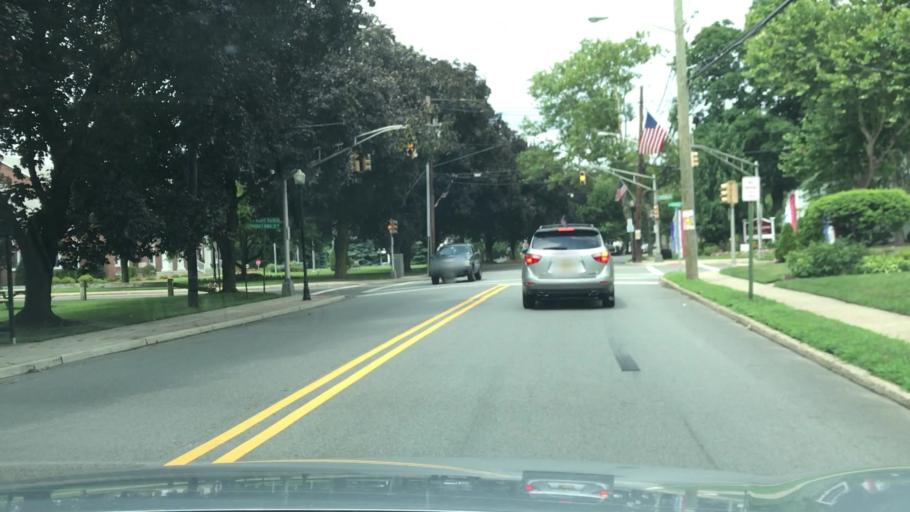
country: US
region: New Jersey
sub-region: Bergen County
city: River Edge
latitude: 40.9232
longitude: -74.0272
